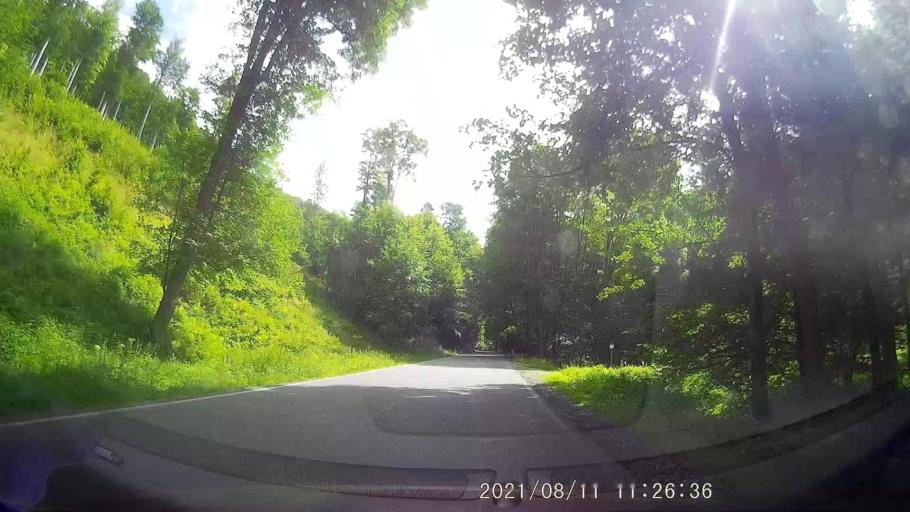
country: PL
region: Lower Silesian Voivodeship
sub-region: Powiat klodzki
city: Stronie Slaskie
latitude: 50.2676
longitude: 16.7683
